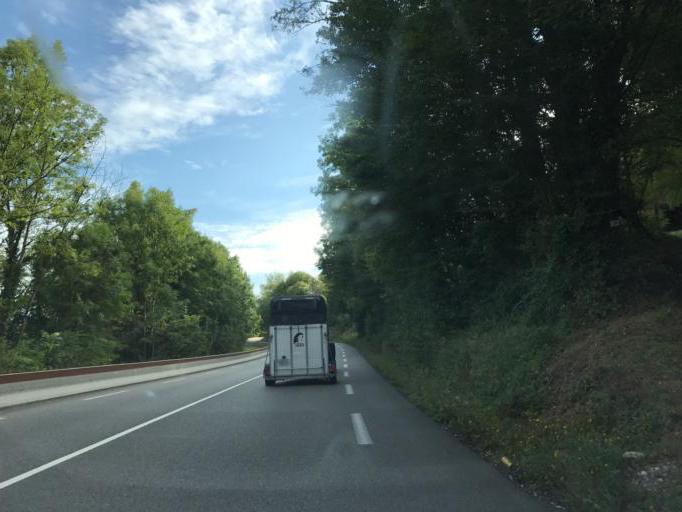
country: FR
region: Rhone-Alpes
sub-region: Departement de l'Ain
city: Collonges
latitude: 46.1122
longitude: 5.8795
